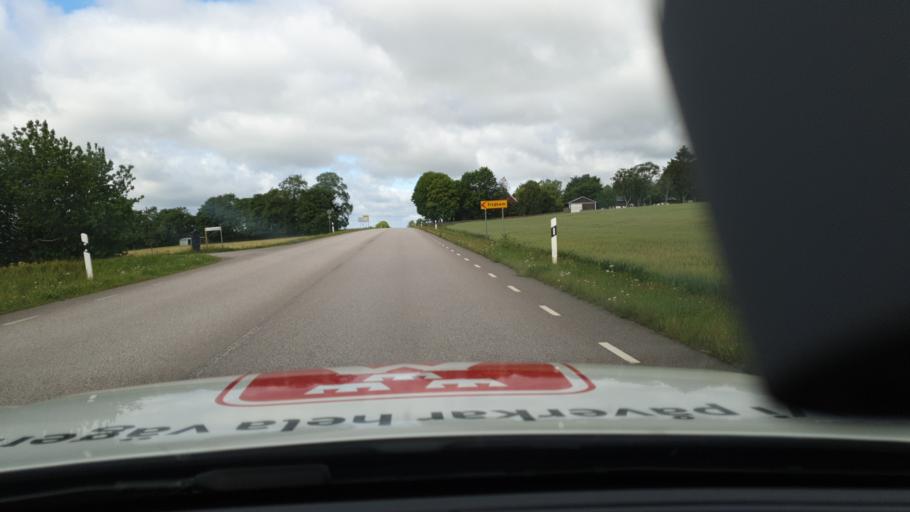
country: SE
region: Vaestra Goetaland
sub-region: Falkopings Kommun
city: Falkoeping
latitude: 58.1618
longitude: 13.5114
